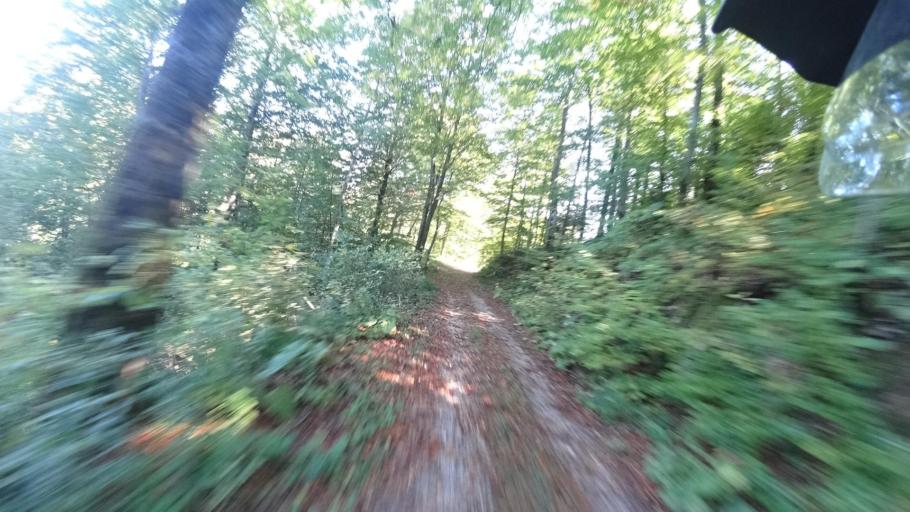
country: HR
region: Karlovacka
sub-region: Grad Ogulin
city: Ogulin
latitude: 45.1767
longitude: 15.1398
